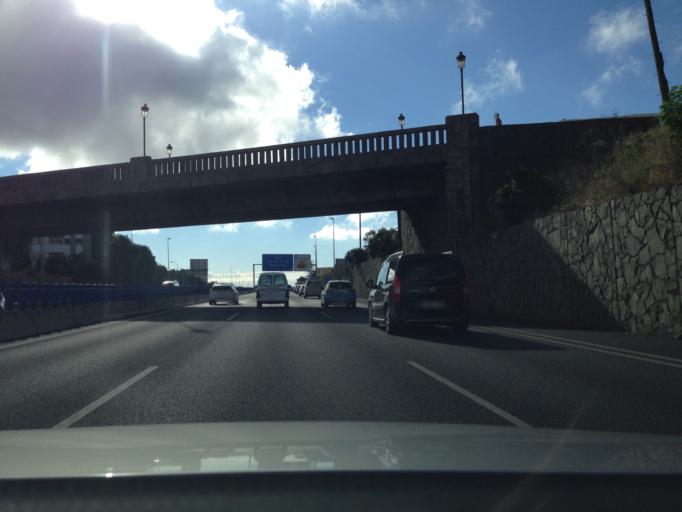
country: ES
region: Canary Islands
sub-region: Provincia de Santa Cruz de Tenerife
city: La Laguna
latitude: 28.4848
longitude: -16.3225
